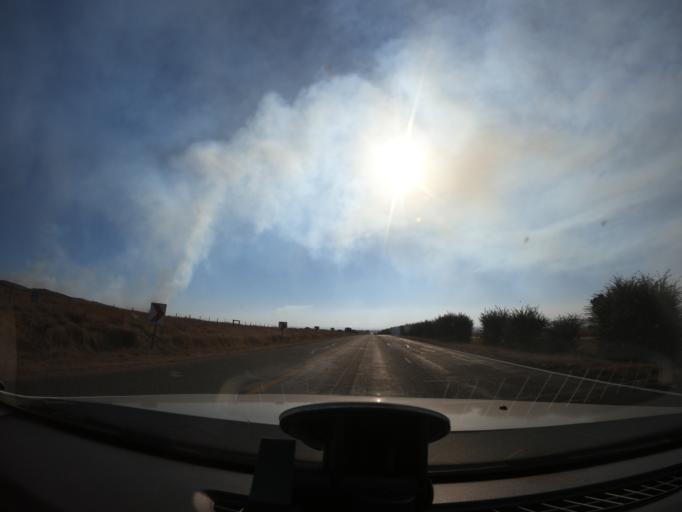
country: ZA
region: Gauteng
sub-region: Sedibeng District Municipality
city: Heidelberg
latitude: -26.4615
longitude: 28.3311
